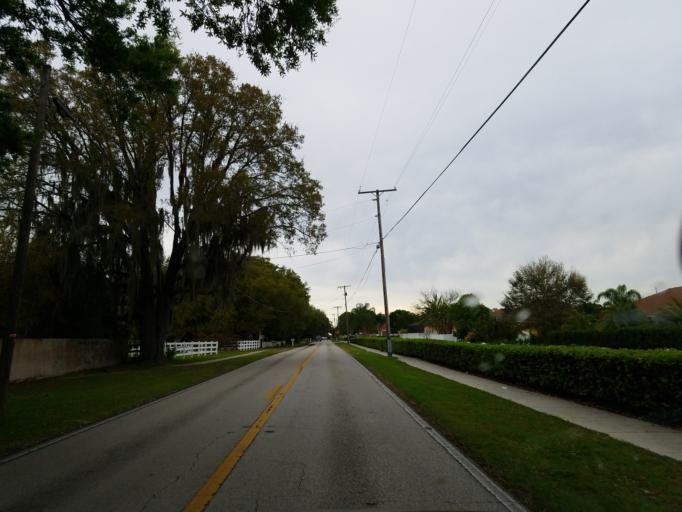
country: US
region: Florida
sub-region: Hillsborough County
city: Valrico
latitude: 27.9201
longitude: -82.2444
